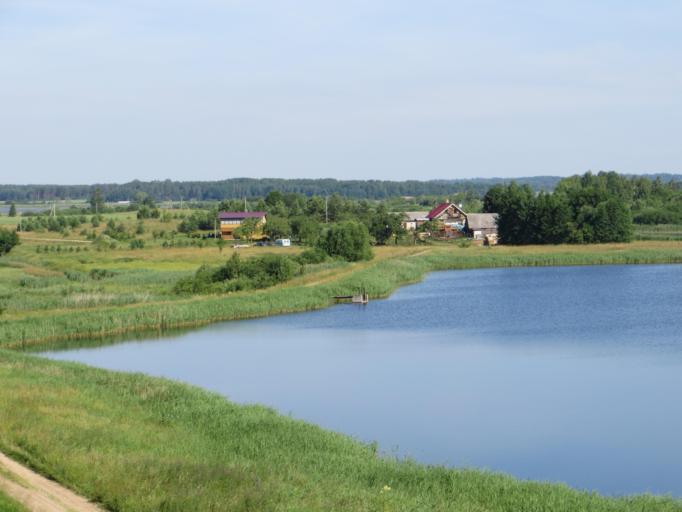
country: LT
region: Alytaus apskritis
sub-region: Alytaus rajonas
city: Daugai
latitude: 54.3939
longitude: 24.4256
